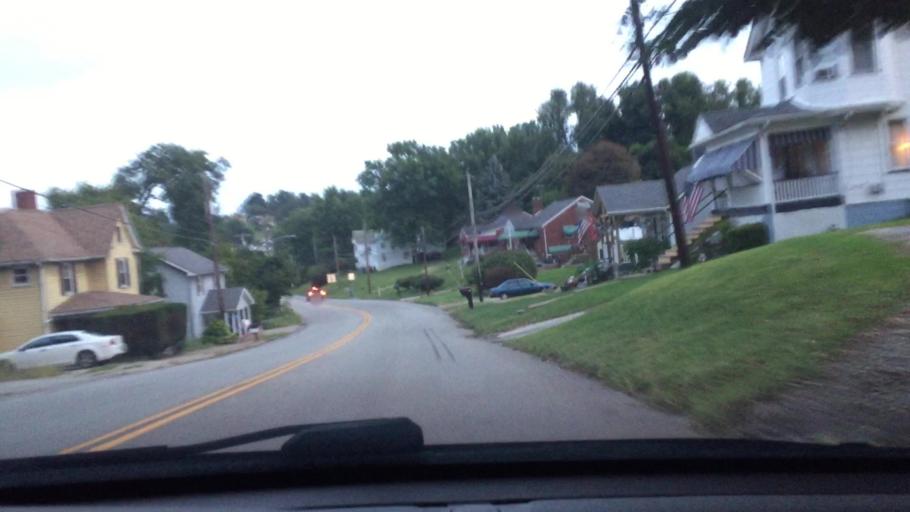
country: US
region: Pennsylvania
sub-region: Washington County
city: East Washington
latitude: 40.1545
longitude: -80.2132
